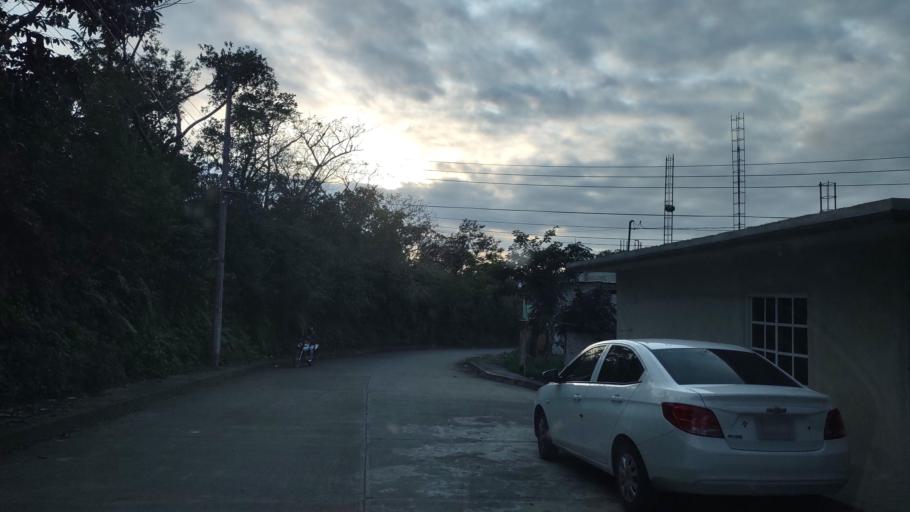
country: MX
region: Veracruz
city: Papantla de Olarte
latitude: 20.4560
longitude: -97.3051
